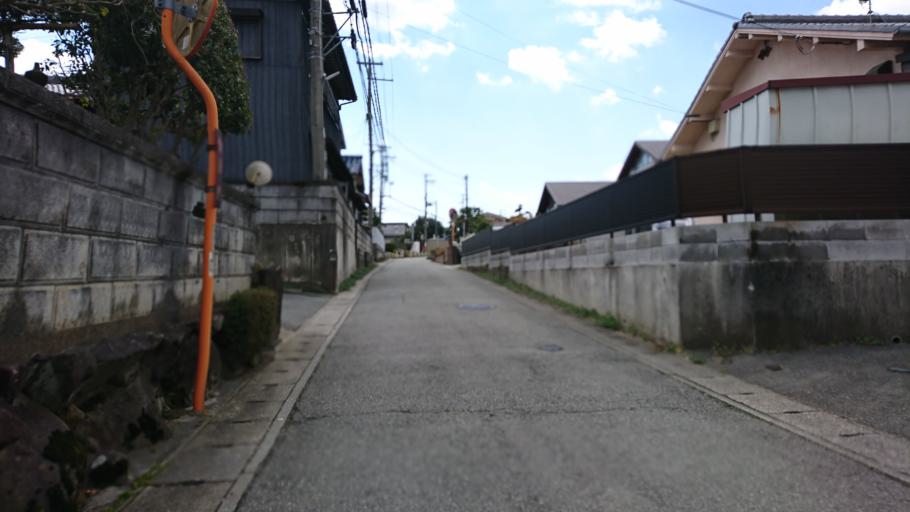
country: JP
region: Hyogo
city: Miki
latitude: 34.7618
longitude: 134.9548
